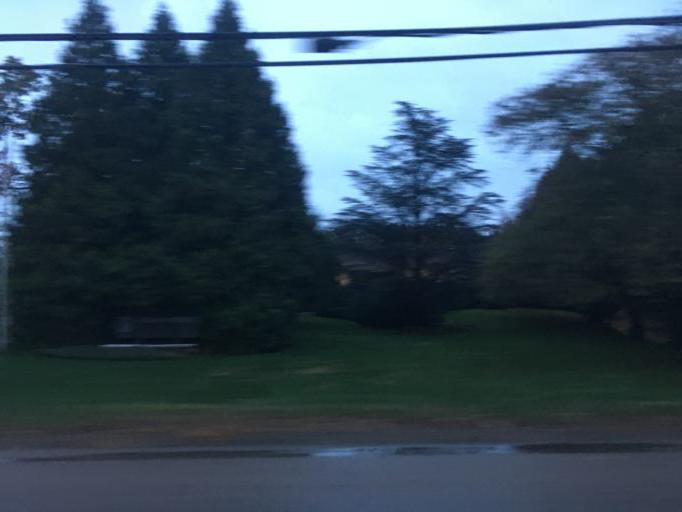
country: US
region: Rhode Island
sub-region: Kent County
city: East Greenwich
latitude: 41.6548
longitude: -71.4971
